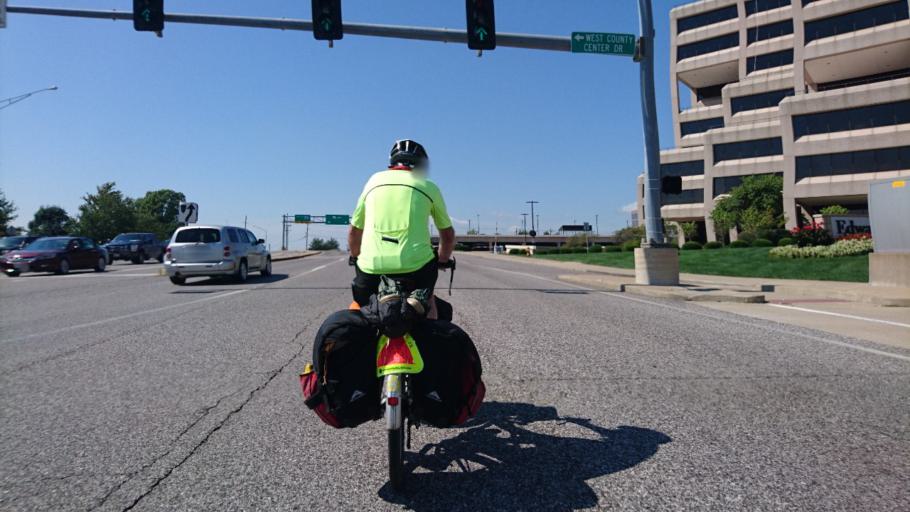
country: US
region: Missouri
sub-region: Saint Louis County
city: Des Peres
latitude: 38.6037
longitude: -90.4464
